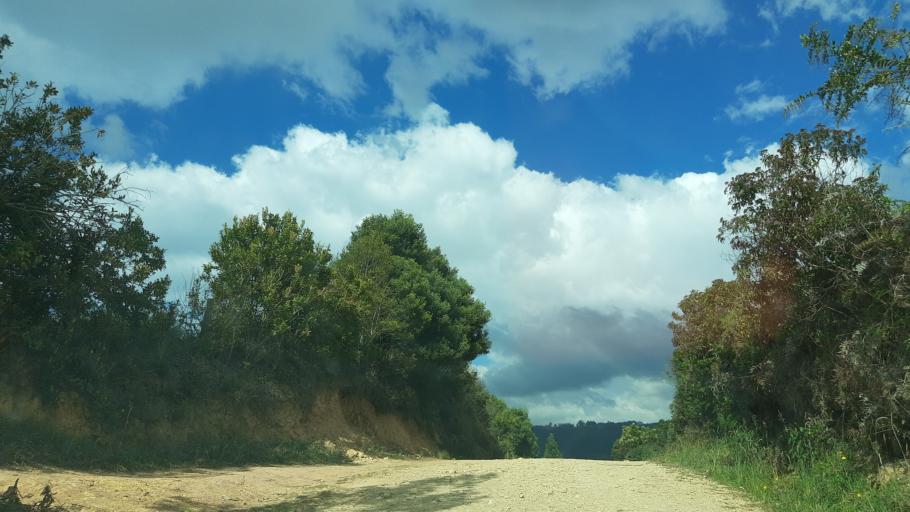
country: CO
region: Boyaca
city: Santa Sofia
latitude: 5.7369
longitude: -73.5518
